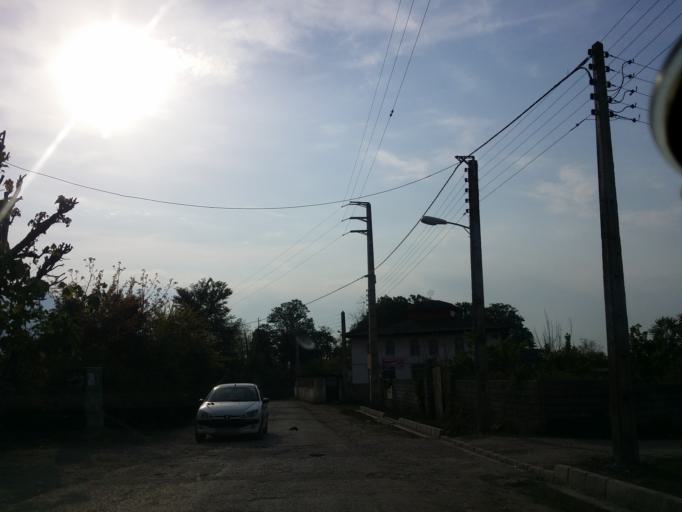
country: IR
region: Mazandaran
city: Chalus
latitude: 36.6576
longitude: 51.3924
